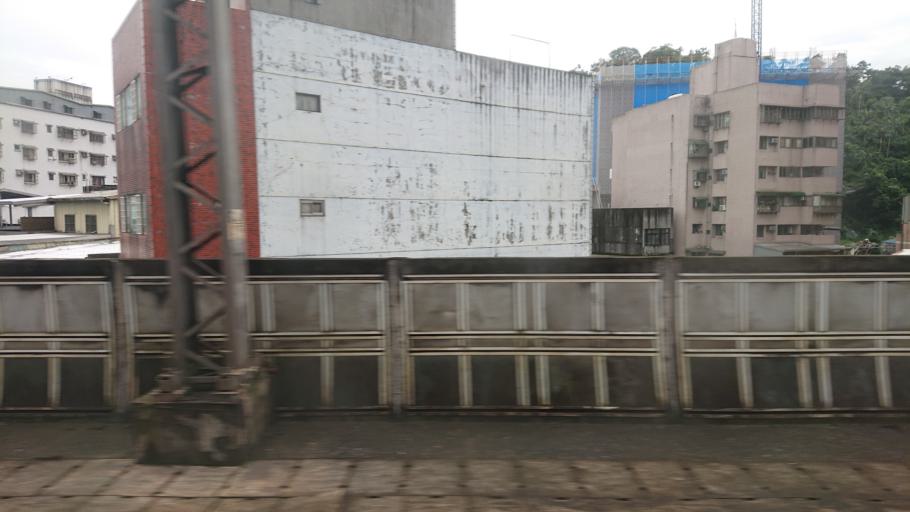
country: TW
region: Taiwan
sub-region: Keelung
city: Keelung
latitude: 25.0754
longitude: 121.6657
